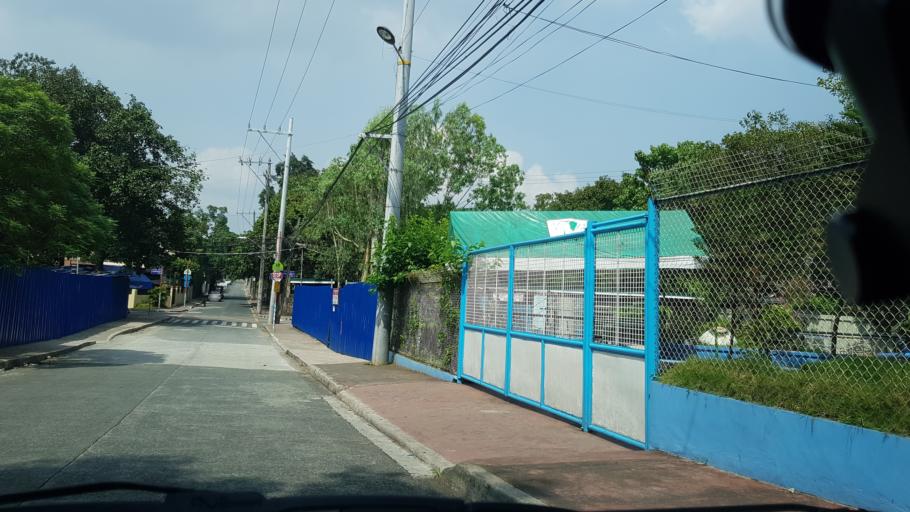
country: PH
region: Calabarzon
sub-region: Province of Rizal
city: Antipolo
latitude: 14.6484
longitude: 121.1188
